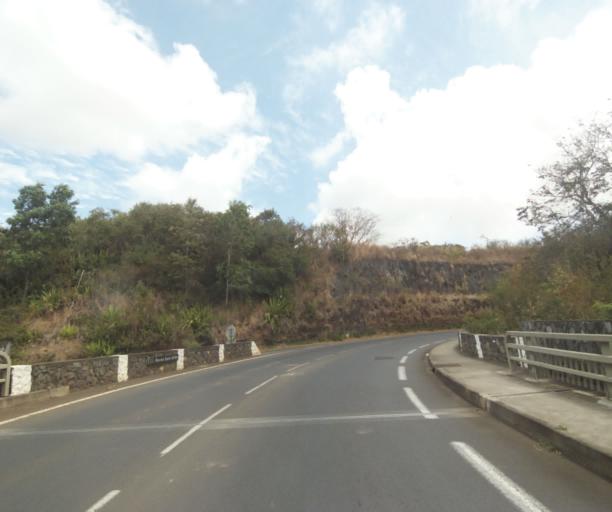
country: RE
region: Reunion
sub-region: Reunion
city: Saint-Paul
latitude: -21.0538
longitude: 55.2683
